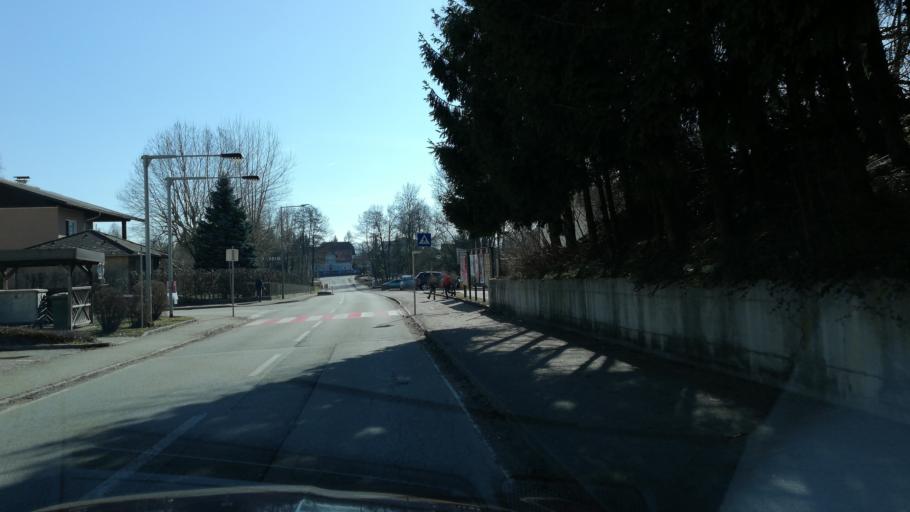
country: AT
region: Upper Austria
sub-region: Politischer Bezirk Vocklabruck
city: Schwanenstadt
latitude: 48.0595
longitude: 13.7788
